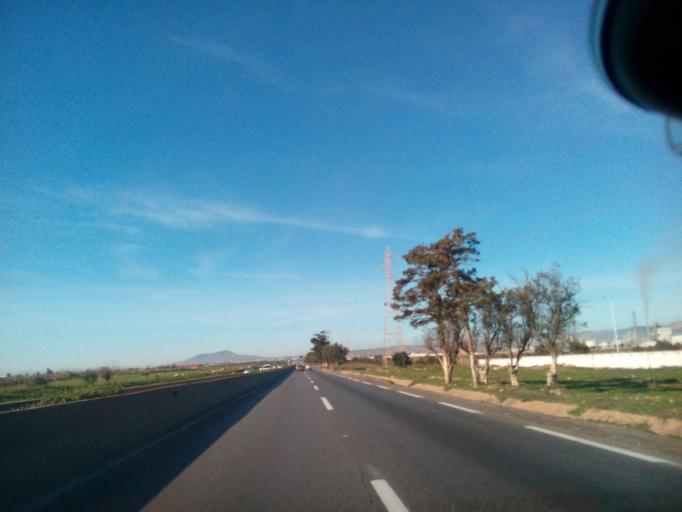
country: DZ
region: Oran
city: Ain el Bya
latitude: 35.8004
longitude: -0.3260
